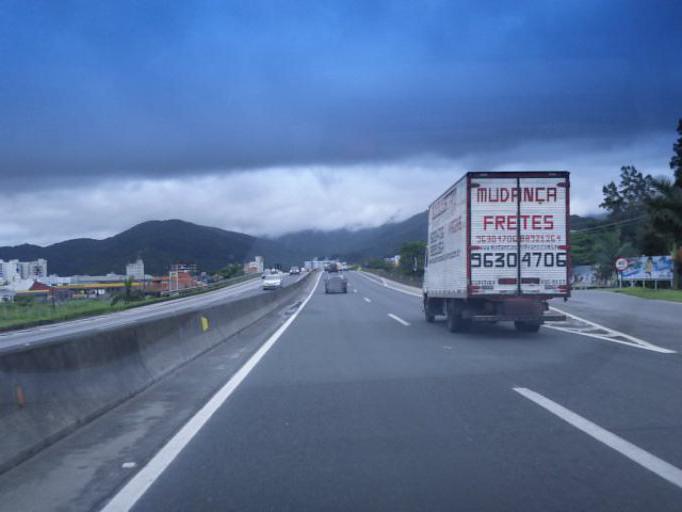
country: BR
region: Santa Catarina
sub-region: Itapema
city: Itapema
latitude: -27.0860
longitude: -48.6083
